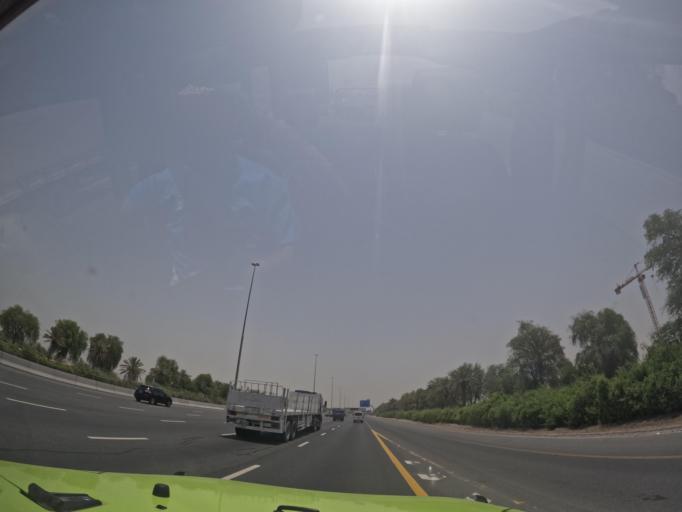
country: AE
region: Dubai
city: Dubai
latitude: 25.1047
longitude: 55.3389
